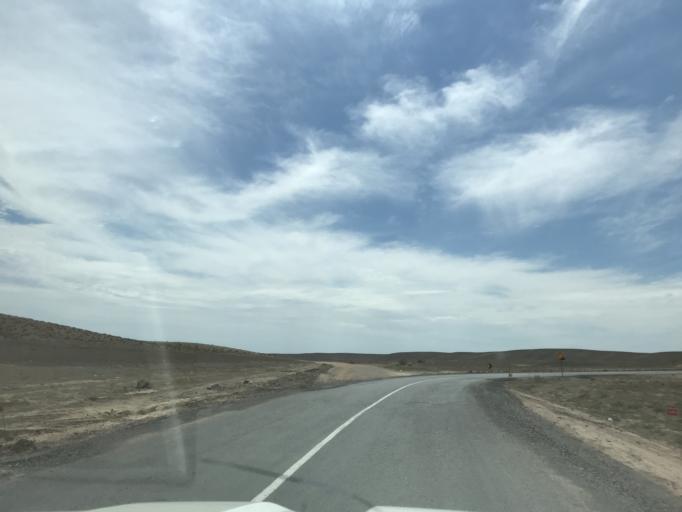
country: KZ
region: Almaty Oblysy
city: Ulken
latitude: 45.0607
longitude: 74.0035
